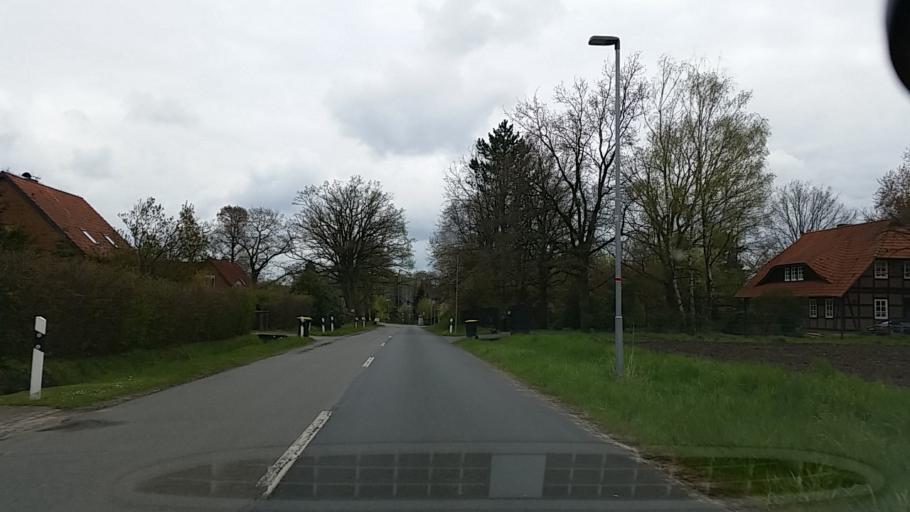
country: DE
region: Lower Saxony
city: Eldingen
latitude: 52.6561
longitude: 10.3286
